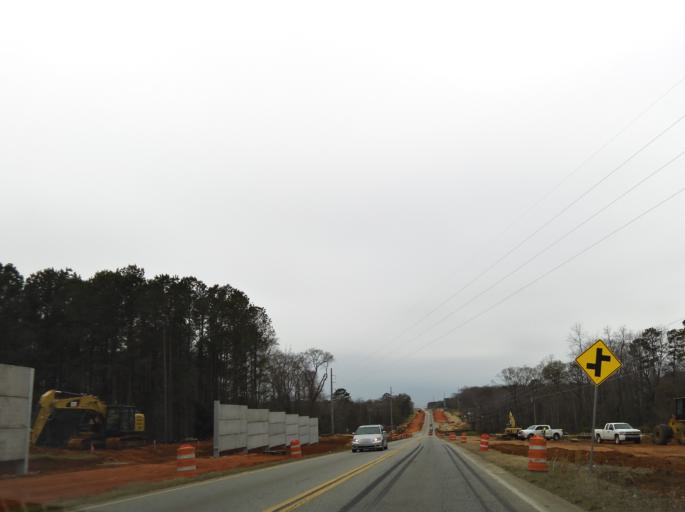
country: US
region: Georgia
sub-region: Houston County
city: Centerville
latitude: 32.5466
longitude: -83.7100
